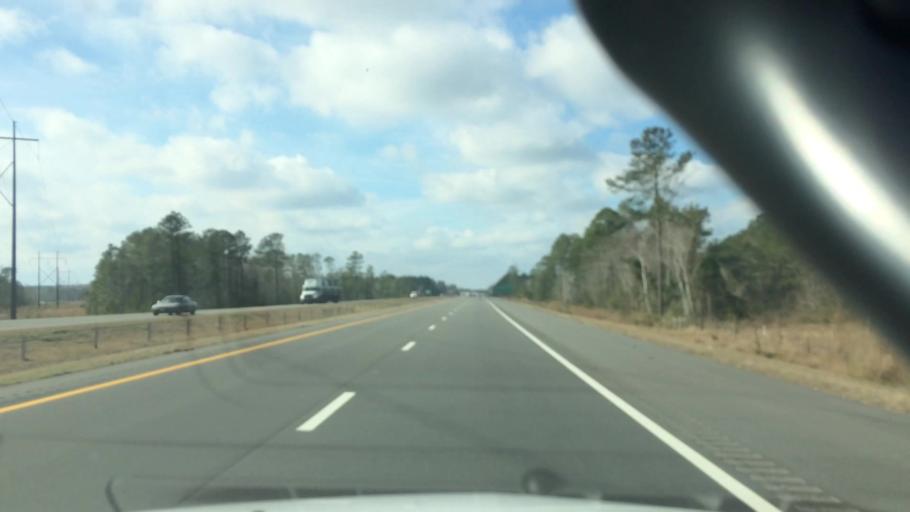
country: US
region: North Carolina
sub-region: Brunswick County
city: Leland
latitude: 34.2743
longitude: -78.0352
